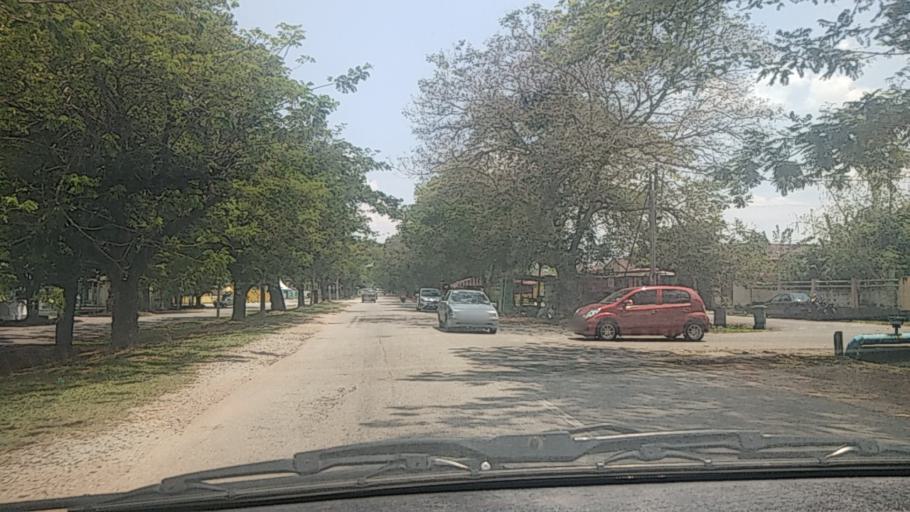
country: MY
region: Kedah
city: Sungai Petani
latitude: 5.6459
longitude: 100.5233
